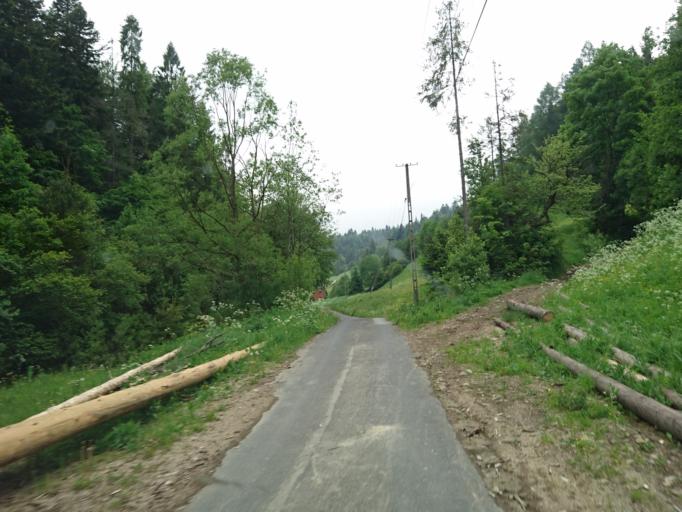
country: PL
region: Lesser Poland Voivodeship
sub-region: Powiat limanowski
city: Lubomierz
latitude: 49.5366
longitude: 20.2013
